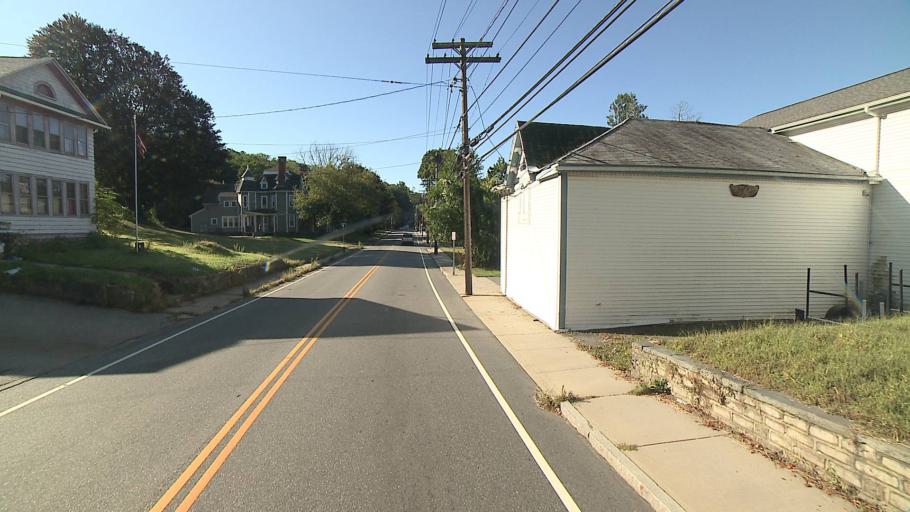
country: US
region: Connecticut
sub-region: New London County
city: Norwich
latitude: 41.5191
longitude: -72.0751
